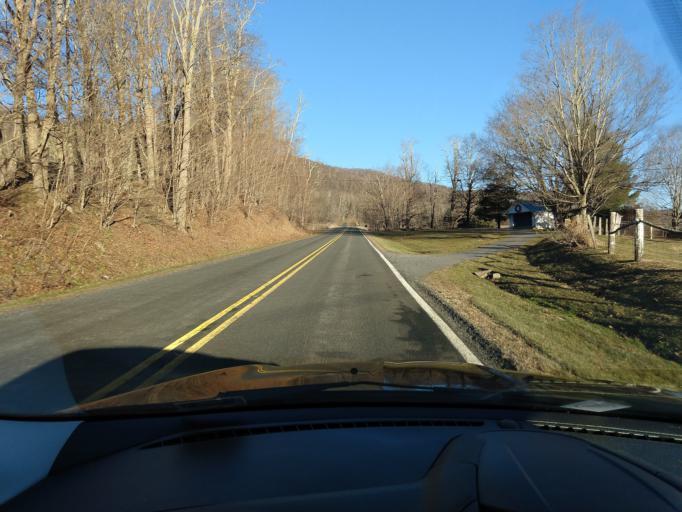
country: US
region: Virginia
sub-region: Highland County
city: Monterey
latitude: 38.4354
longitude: -79.6378
